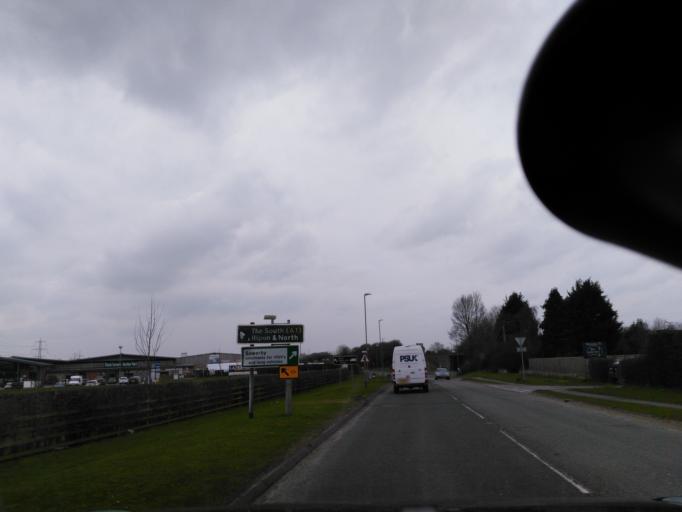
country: GB
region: England
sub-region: North Yorkshire
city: Thirsk
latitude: 54.2255
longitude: -1.3247
